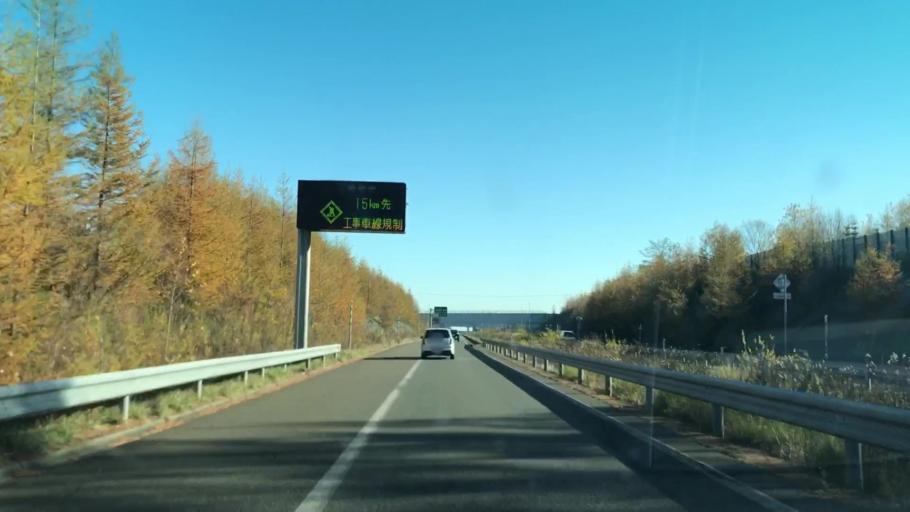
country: JP
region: Hokkaido
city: Otofuke
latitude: 42.9988
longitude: 142.8518
